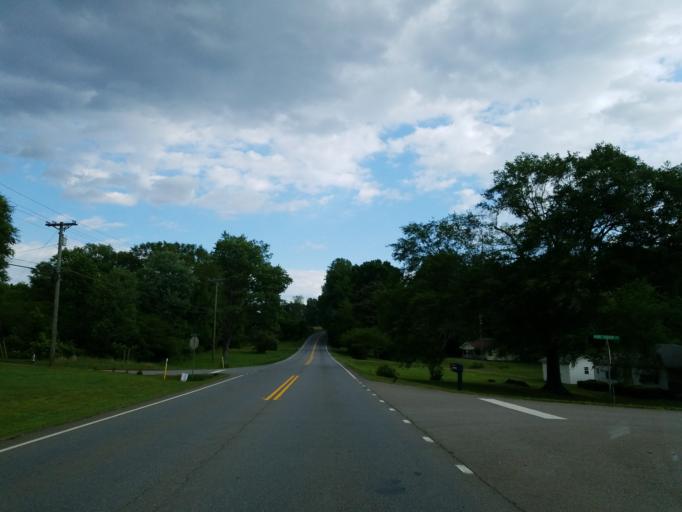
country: US
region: Georgia
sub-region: Cherokee County
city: Ball Ground
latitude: 34.2544
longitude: -84.2868
